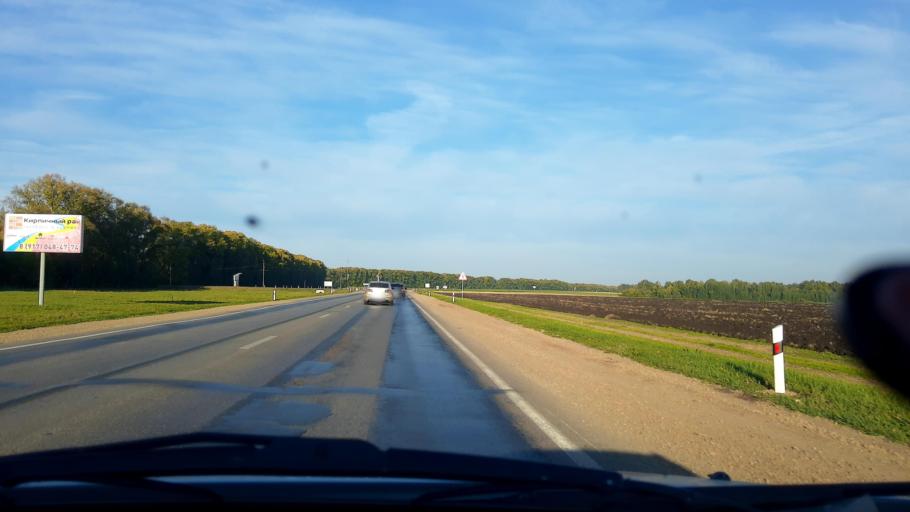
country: RU
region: Bashkortostan
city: Karmaskaly
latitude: 54.3852
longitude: 56.1561
